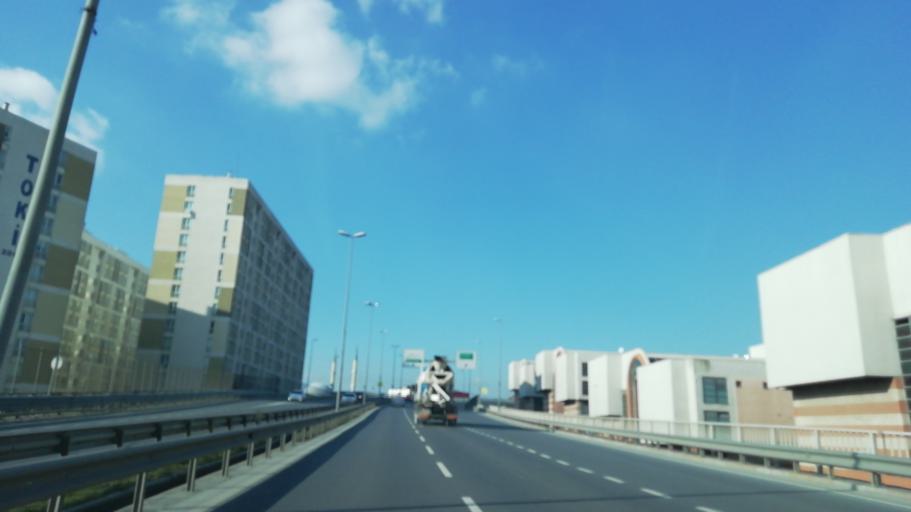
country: TR
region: Istanbul
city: Esenler
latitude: 41.0658
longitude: 28.8626
